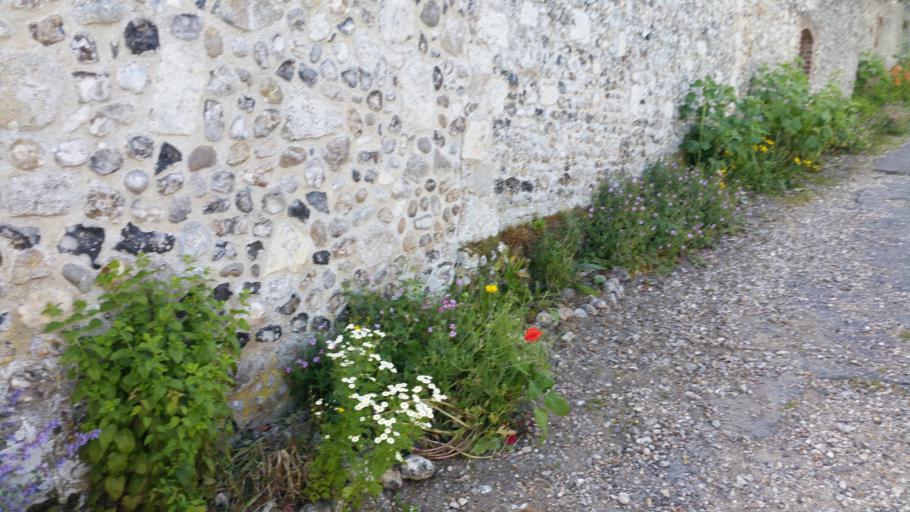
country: FR
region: Picardie
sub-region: Departement de la Somme
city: Saint-Valery-sur-Somme
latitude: 50.1875
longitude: 1.6279
